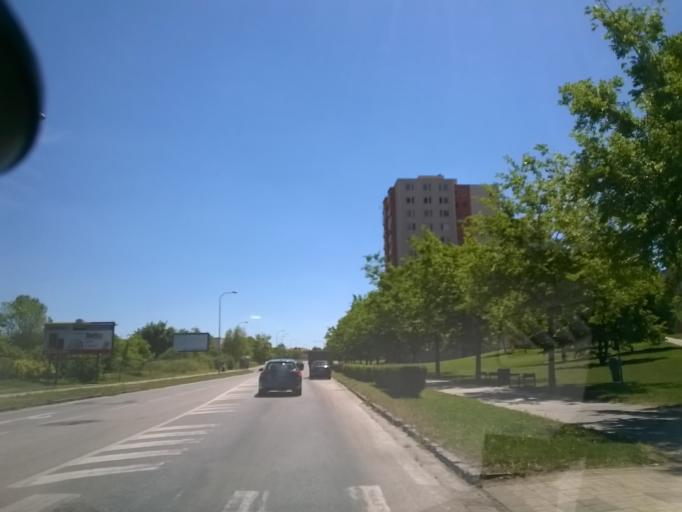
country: SK
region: Nitriansky
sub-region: Okres Nitra
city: Nitra
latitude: 48.3006
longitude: 18.0645
